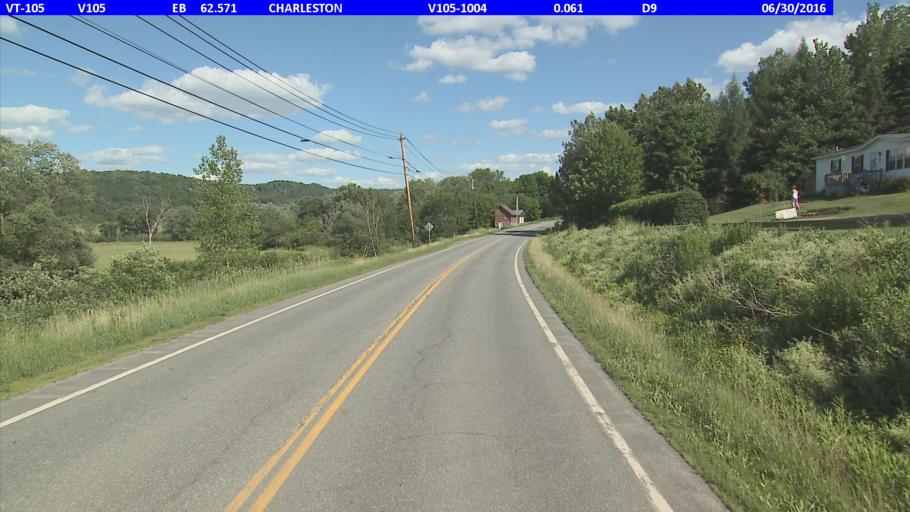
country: US
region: Vermont
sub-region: Orleans County
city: Newport
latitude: 44.9050
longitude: -72.0756
